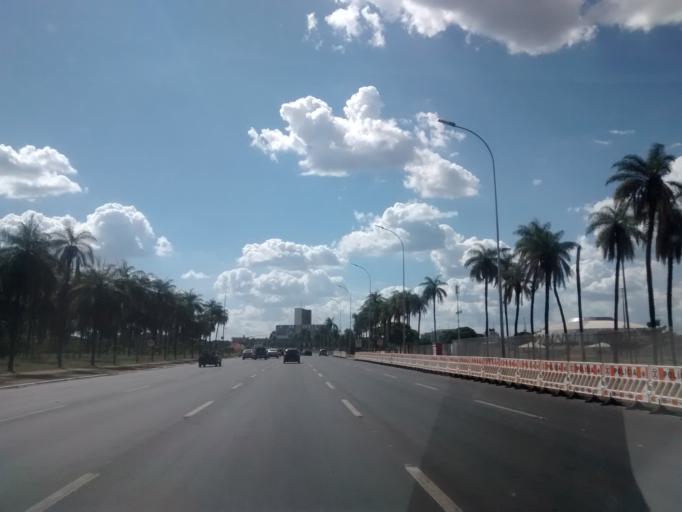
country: BR
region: Federal District
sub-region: Brasilia
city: Brasilia
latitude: -15.7866
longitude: -47.8992
